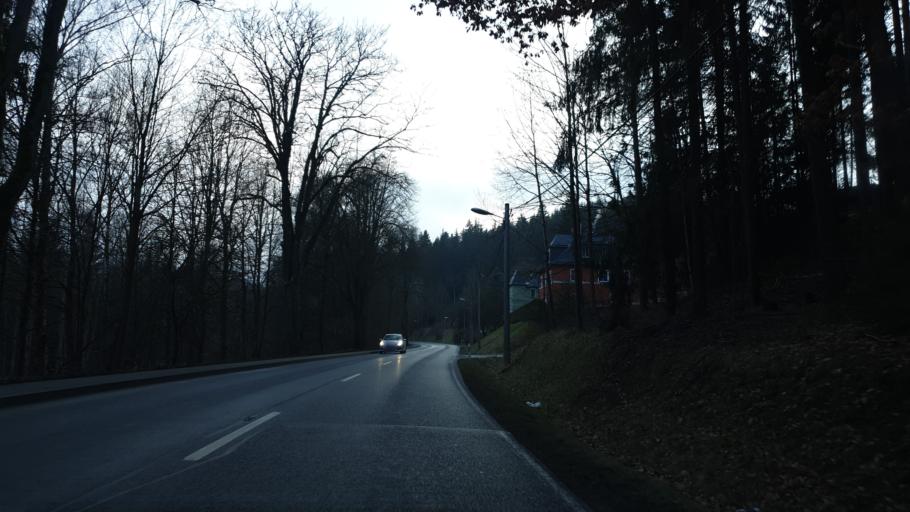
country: DE
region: Saxony
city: Bad Elster
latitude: 50.2945
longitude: 12.2462
